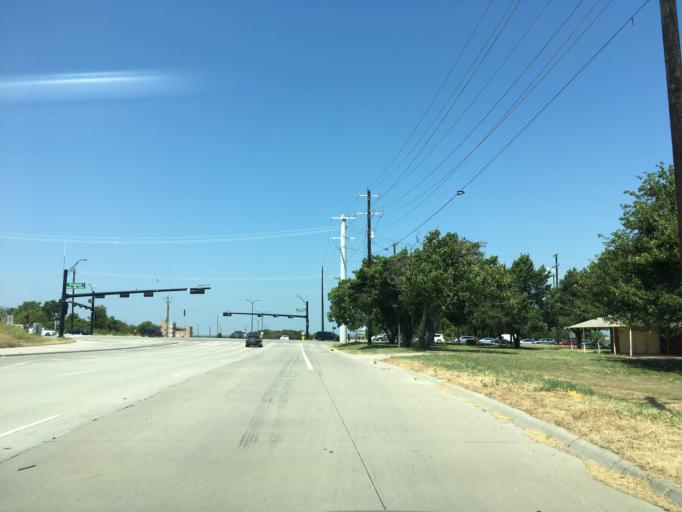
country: US
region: Texas
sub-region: Collin County
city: Prosper
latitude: 33.2042
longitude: -96.8016
